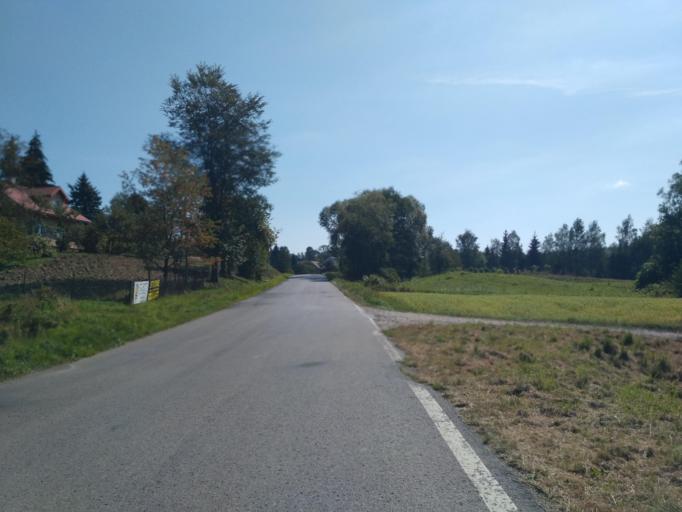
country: PL
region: Subcarpathian Voivodeship
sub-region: Powiat brzozowski
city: Niebocko
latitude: 49.6575
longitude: 22.1348
